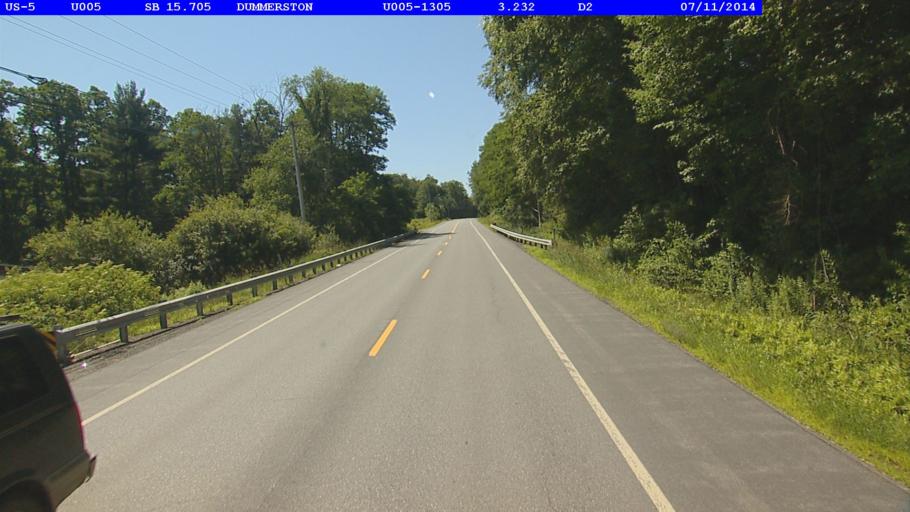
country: US
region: New Hampshire
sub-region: Cheshire County
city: Chesterfield
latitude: 42.9392
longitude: -72.5355
